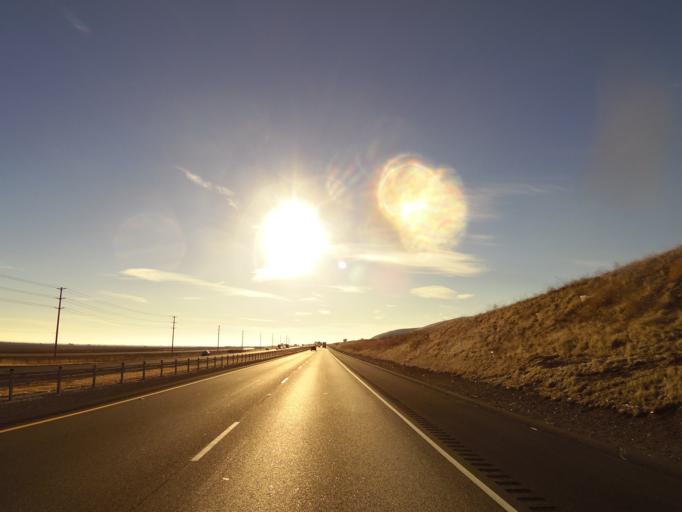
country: US
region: California
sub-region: Stanislaus County
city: Patterson
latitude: 37.5017
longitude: -121.2216
